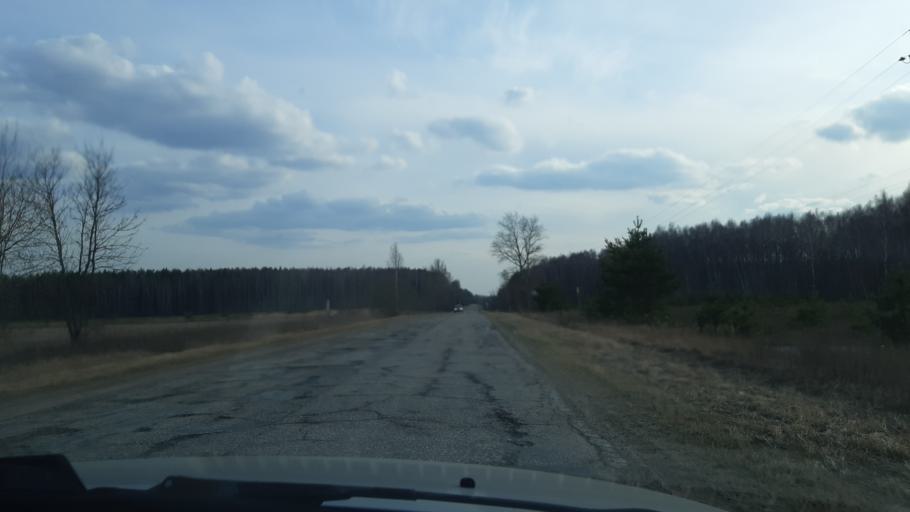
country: RU
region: Vladimir
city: Nikologory
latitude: 56.1220
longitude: 41.9872
